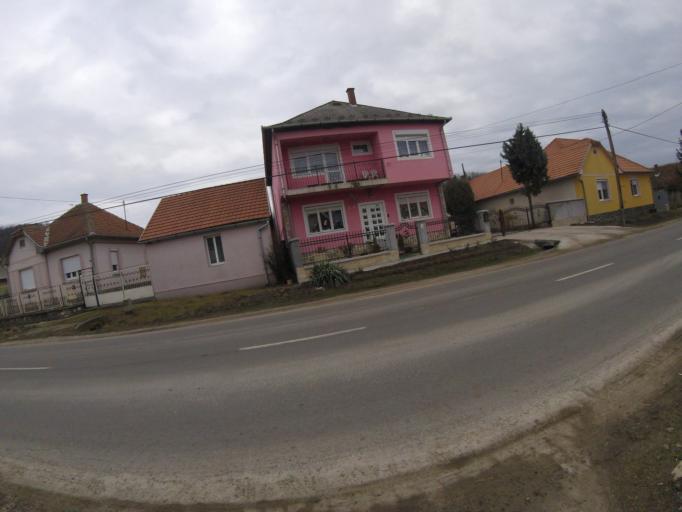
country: HU
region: Heves
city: Kerecsend
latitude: 47.8290
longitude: 20.3329
